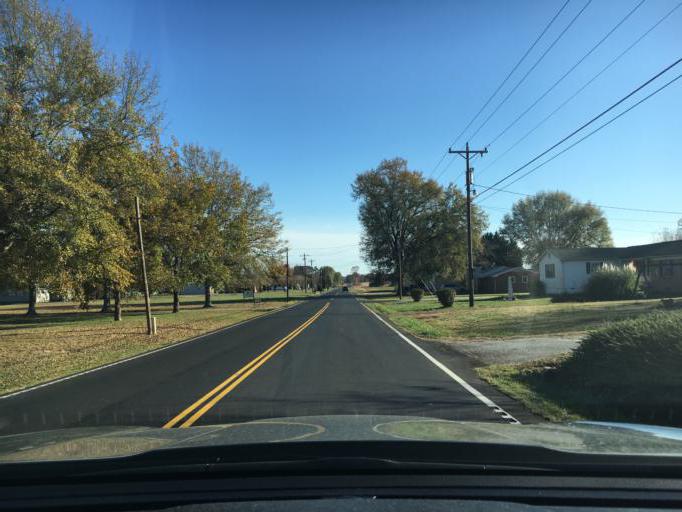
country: US
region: South Carolina
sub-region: Spartanburg County
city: Inman Mills
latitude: 35.0479
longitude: -82.1376
